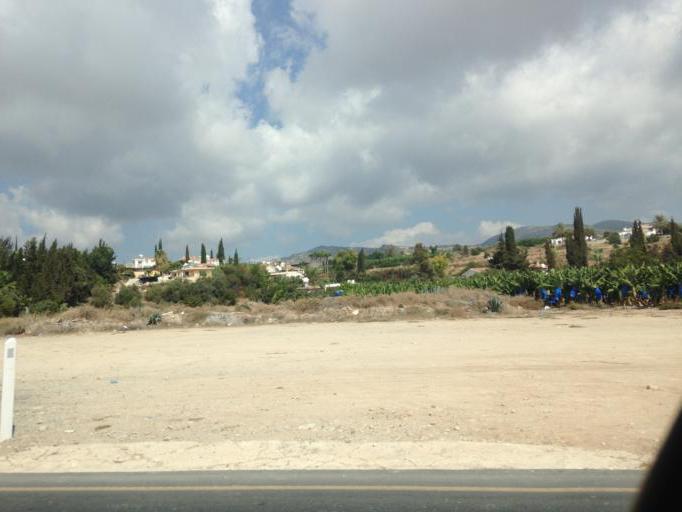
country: CY
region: Pafos
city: Pegeia
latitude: 34.8650
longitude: 32.3786
